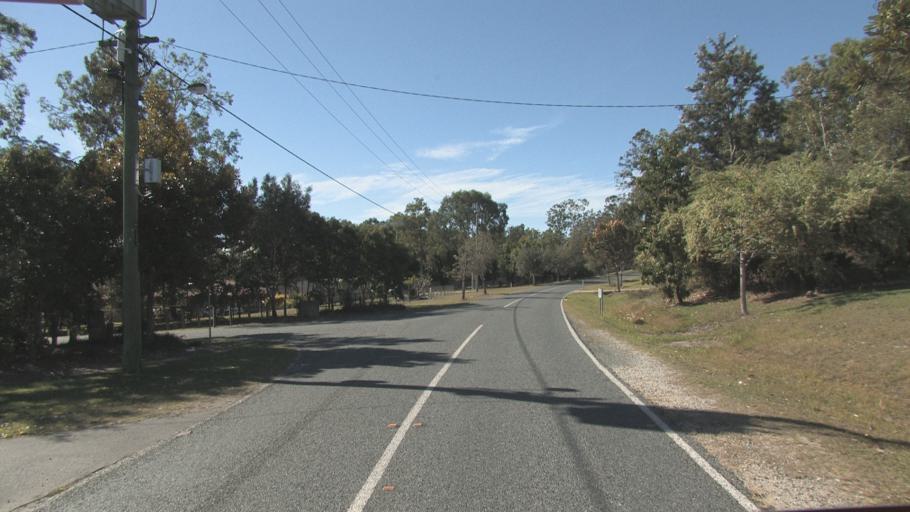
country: AU
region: Queensland
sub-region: Logan
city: North Maclean
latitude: -27.7421
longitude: 152.9562
